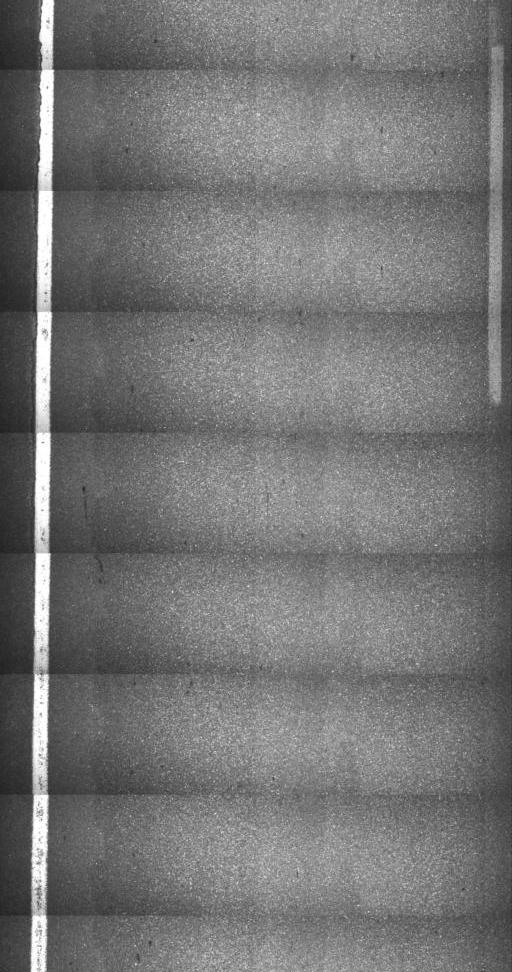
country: US
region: Vermont
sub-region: Orleans County
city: Newport
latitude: 44.8146
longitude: -72.3311
